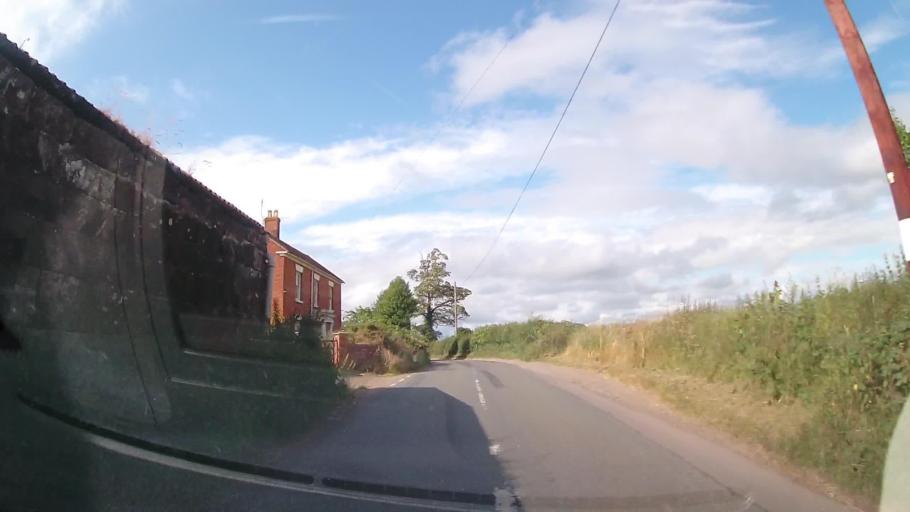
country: GB
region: England
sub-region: Shropshire
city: Petton
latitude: 52.8403
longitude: -2.8045
